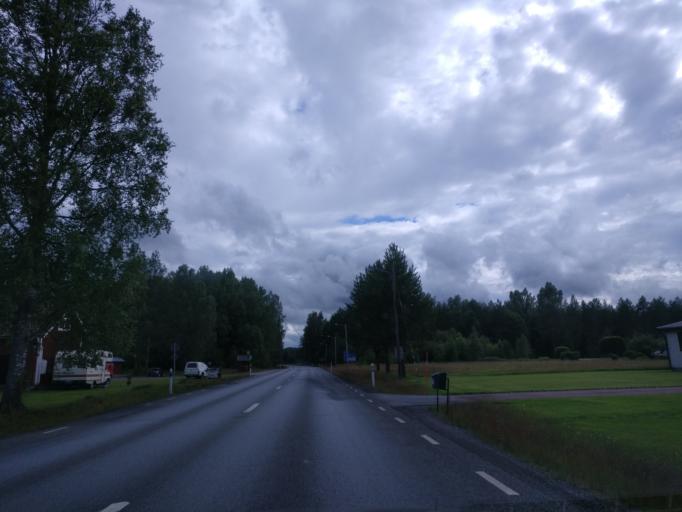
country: SE
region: Vaermland
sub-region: Hagfors Kommun
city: Hagfors
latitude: 59.9698
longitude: 13.5626
